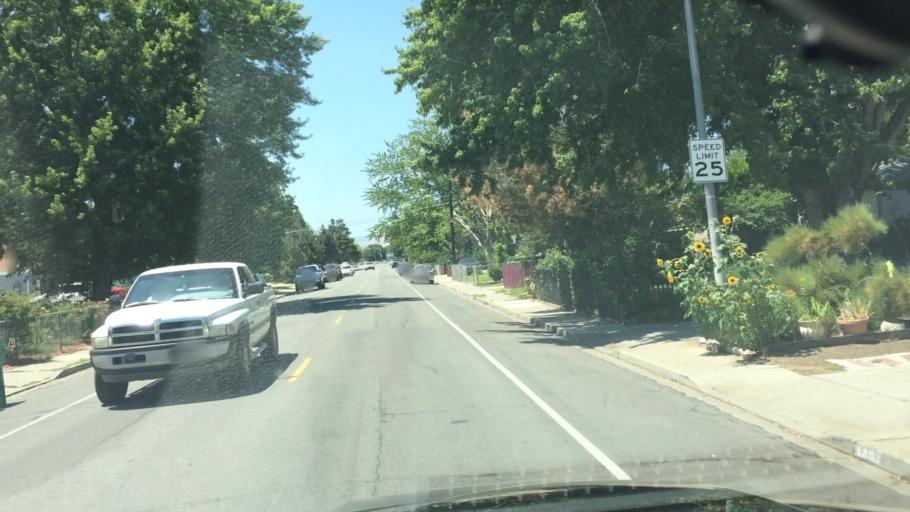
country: US
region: Nevada
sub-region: Washoe County
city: Sparks
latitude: 39.5474
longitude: -119.7454
